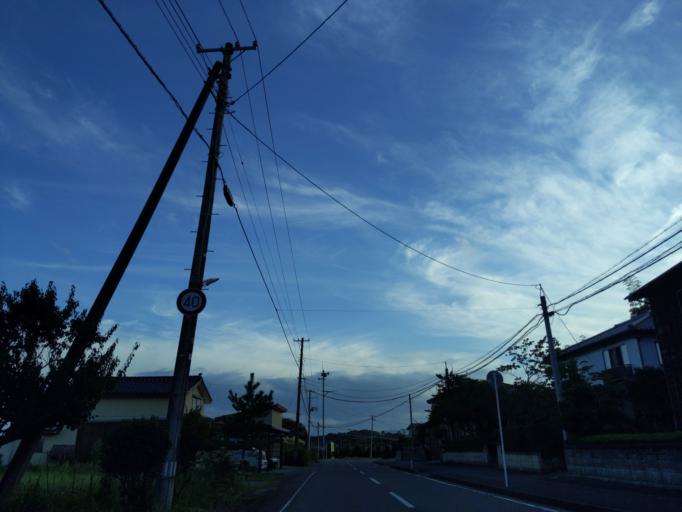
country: JP
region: Niigata
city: Kashiwazaki
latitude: 37.4340
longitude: 138.6226
